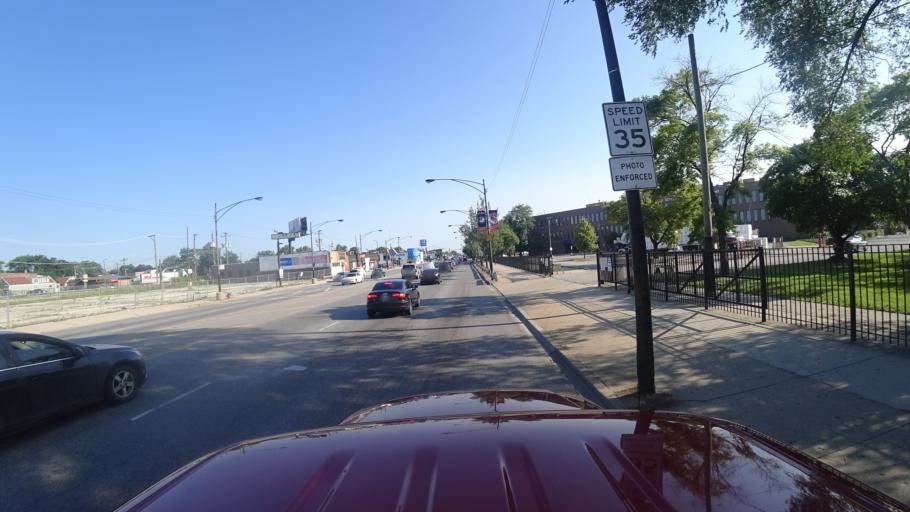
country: US
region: Illinois
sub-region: Cook County
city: Cicero
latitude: 41.8007
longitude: -87.7233
